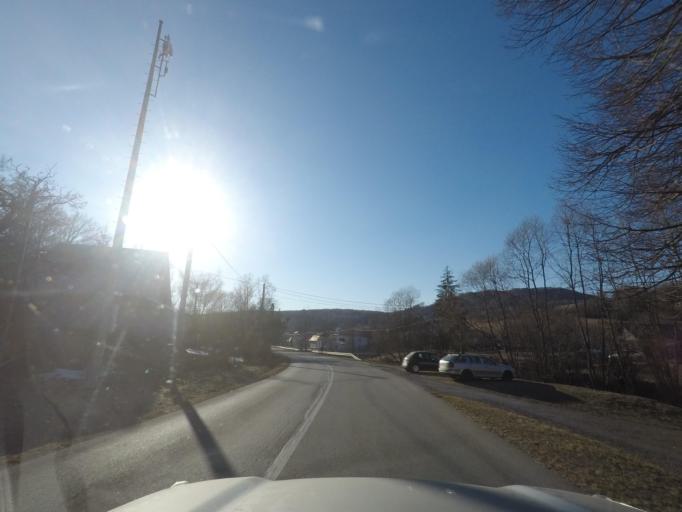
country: SK
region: Presovsky
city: Medzilaborce
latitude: 49.2809
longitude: 21.8264
